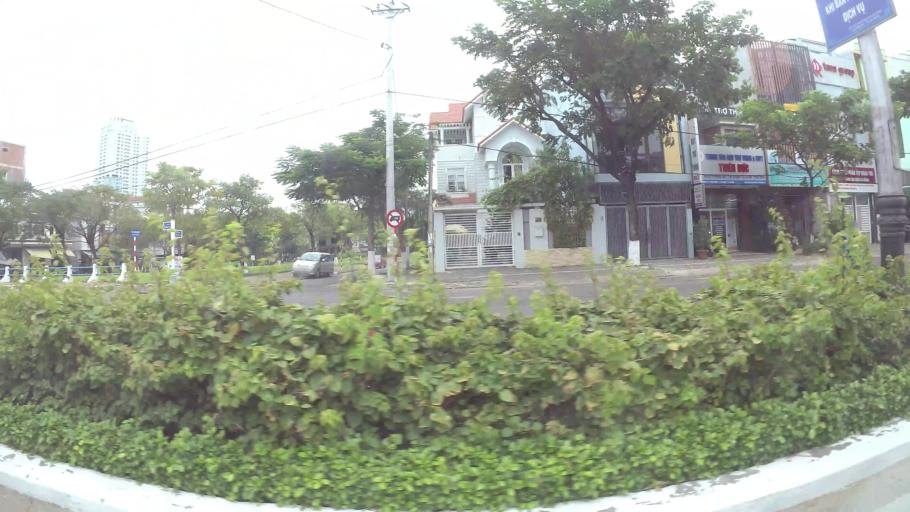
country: VN
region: Da Nang
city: Da Nang
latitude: 16.0866
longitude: 108.2170
